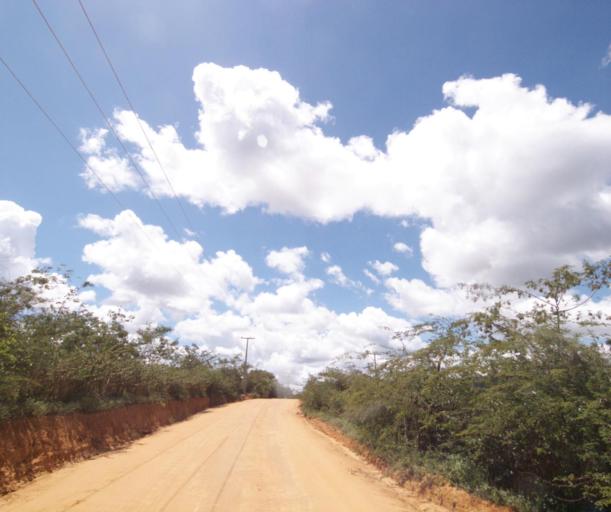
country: BR
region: Bahia
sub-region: Pocoes
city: Pocoes
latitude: -14.3699
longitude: -40.5713
